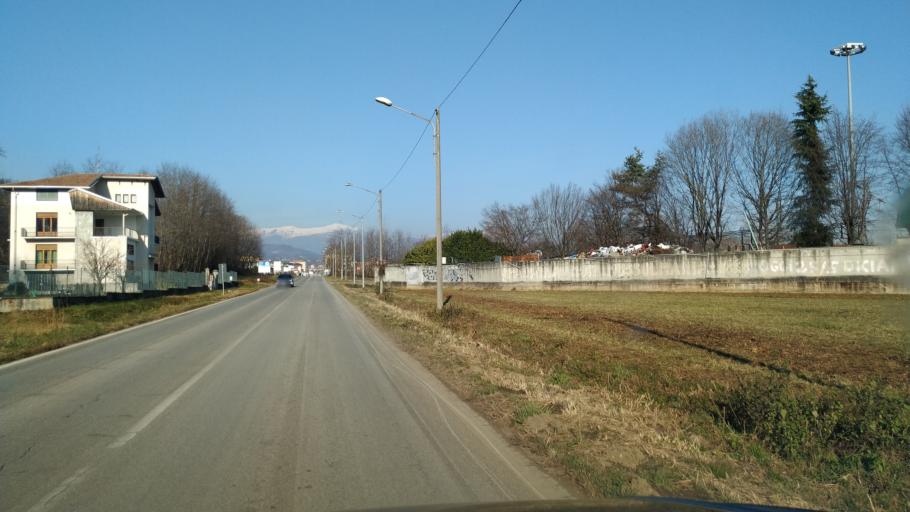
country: IT
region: Piedmont
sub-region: Provincia di Biella
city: Mongrando
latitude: 45.5357
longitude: 8.0115
